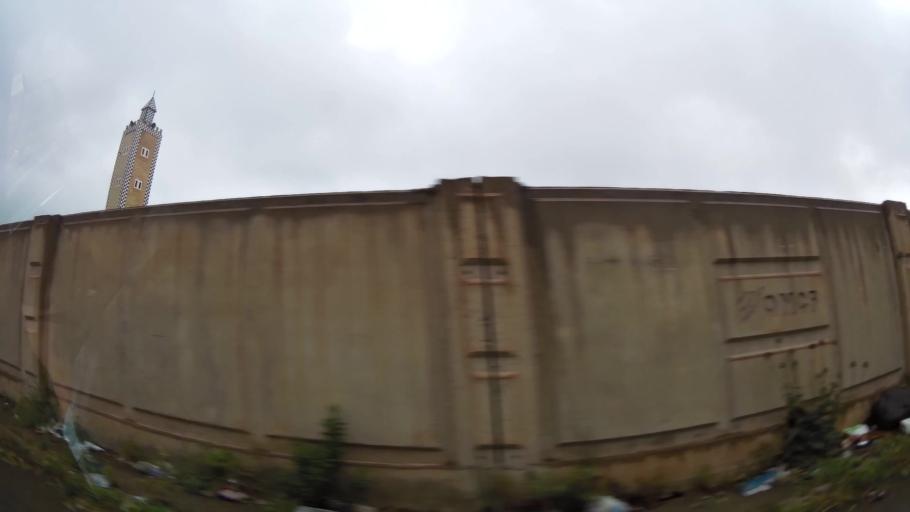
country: MA
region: Oriental
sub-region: Nador
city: Nador
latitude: 35.1603
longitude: -2.9672
